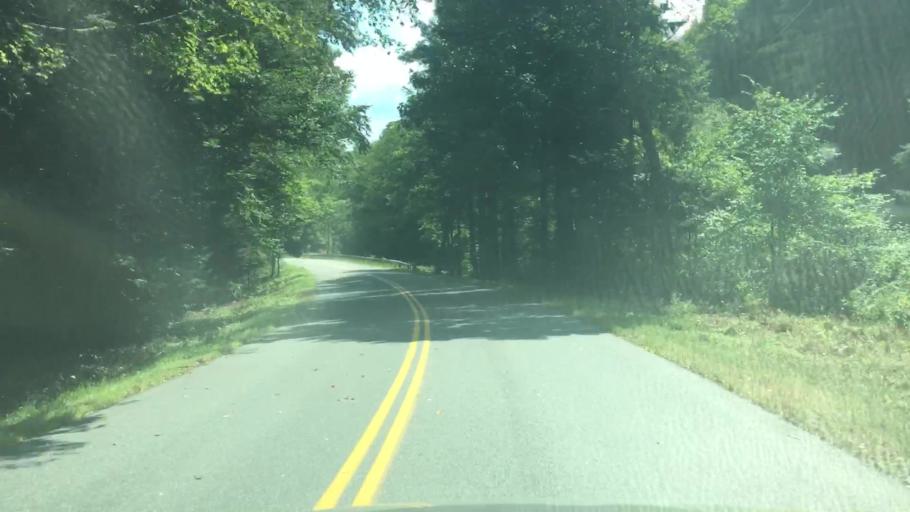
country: US
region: Vermont
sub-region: Windham County
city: West Brattleboro
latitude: 42.8150
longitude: -72.7379
